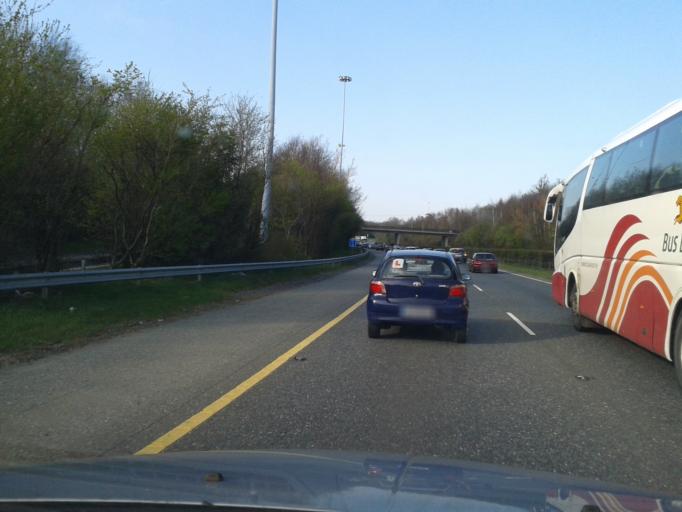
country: IE
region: Leinster
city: Little Bray
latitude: 53.2080
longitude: -6.1252
